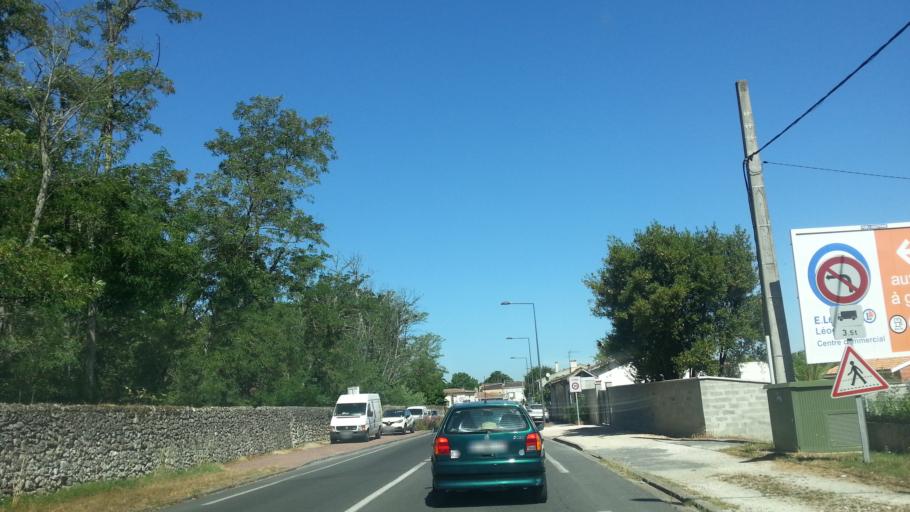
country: FR
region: Aquitaine
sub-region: Departement de la Gironde
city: Cadaujac
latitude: 44.7490
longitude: -0.5468
